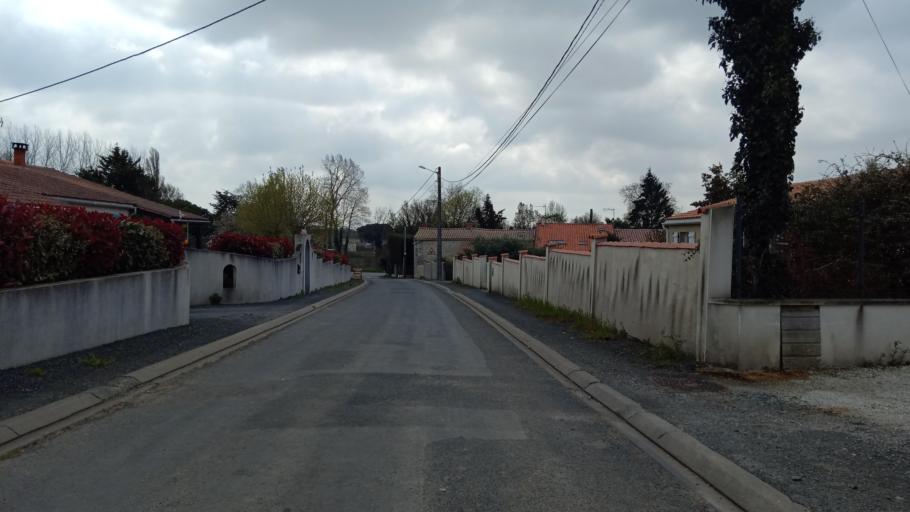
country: FR
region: Poitou-Charentes
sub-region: Departement de la Charente-Maritime
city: Verines
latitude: 46.1547
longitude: -0.9333
